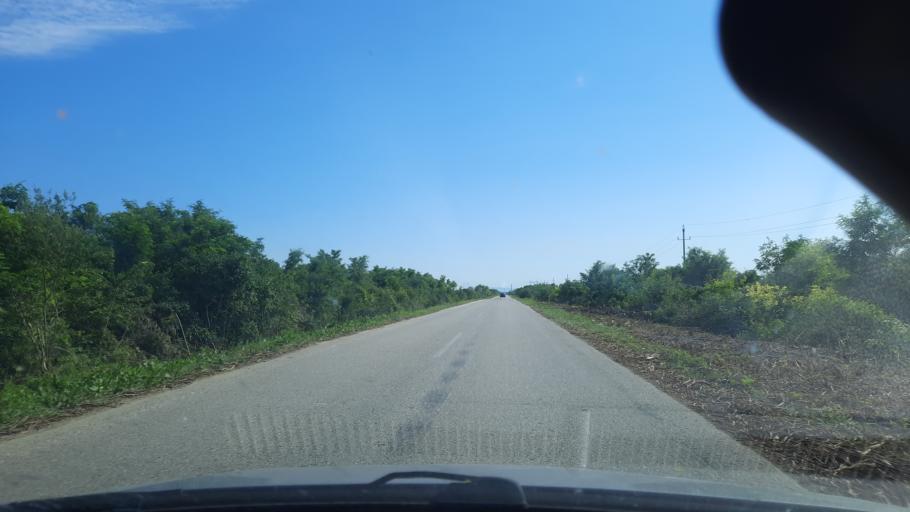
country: RS
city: Simanovci
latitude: 44.7981
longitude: 20.0952
